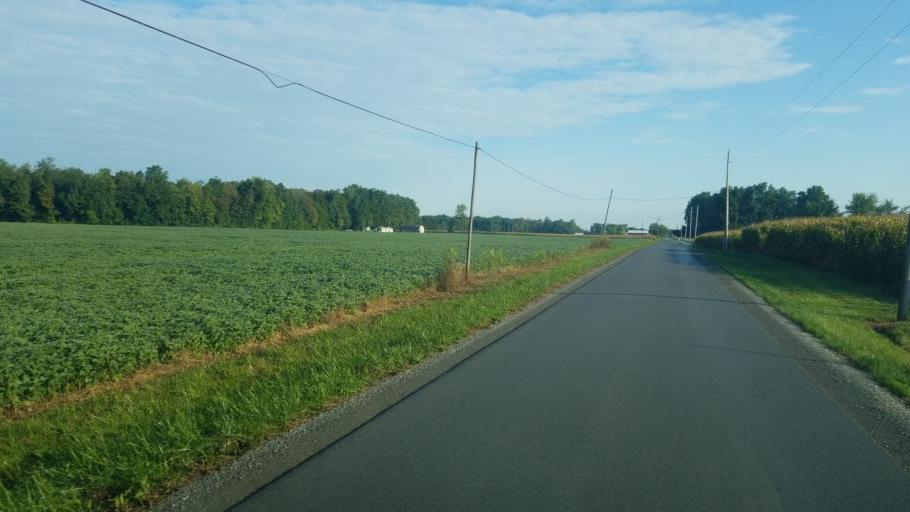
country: US
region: Ohio
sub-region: Morrow County
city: Cardington
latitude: 40.5942
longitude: -82.9379
